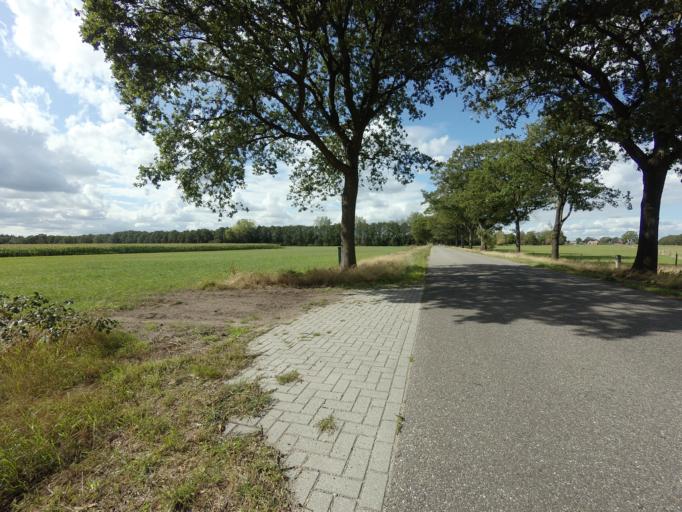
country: NL
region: Friesland
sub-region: Gemeente Heerenveen
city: Jubbega
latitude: 52.9644
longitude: 6.1995
